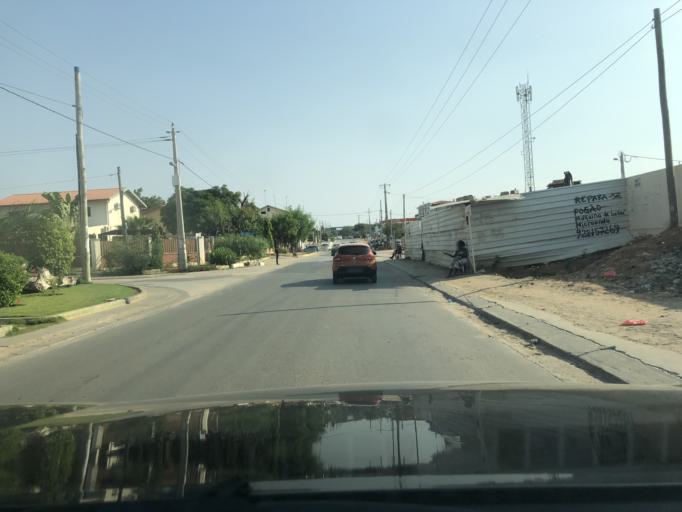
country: AO
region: Luanda
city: Luanda
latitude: -8.9104
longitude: 13.2271
